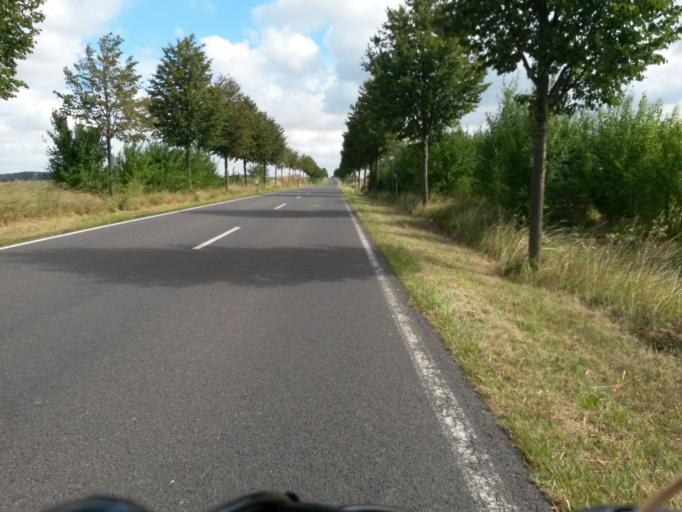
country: DE
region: Brandenburg
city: Angermunde
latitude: 53.0445
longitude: 13.9958
